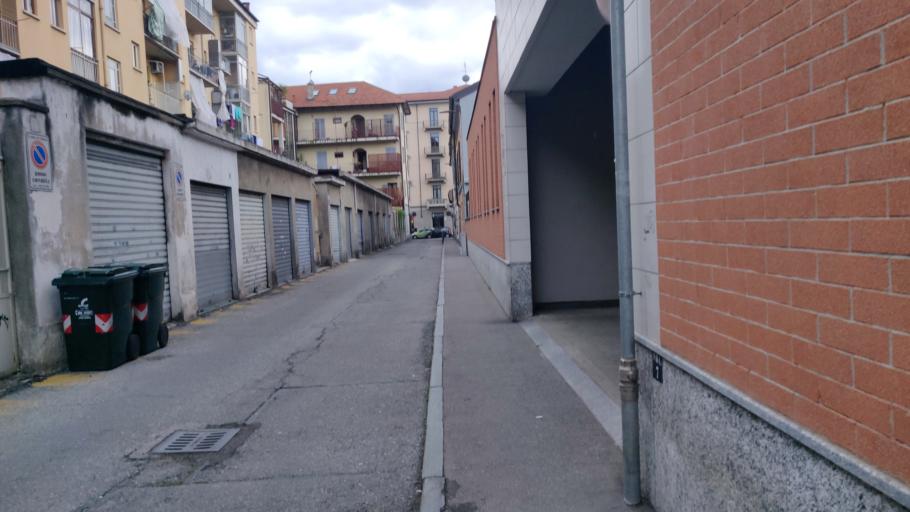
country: IT
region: Piedmont
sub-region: Provincia di Torino
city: Lesna
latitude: 45.0713
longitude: 7.6448
